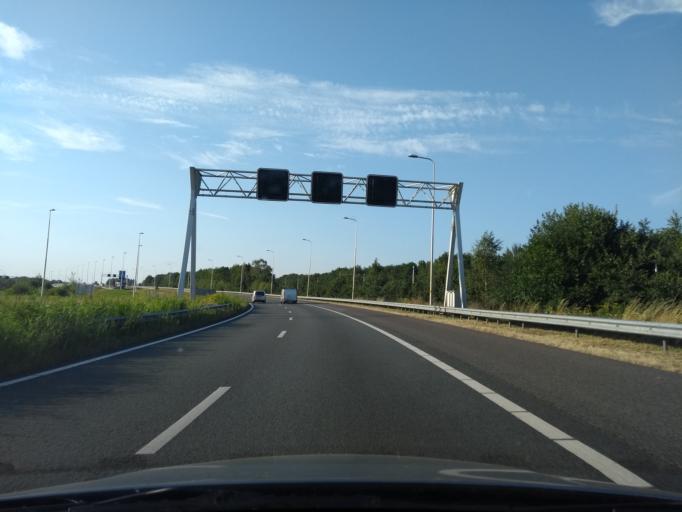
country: NL
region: Overijssel
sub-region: Gemeente Staphorst
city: Staphorst
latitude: 52.6627
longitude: 6.2001
